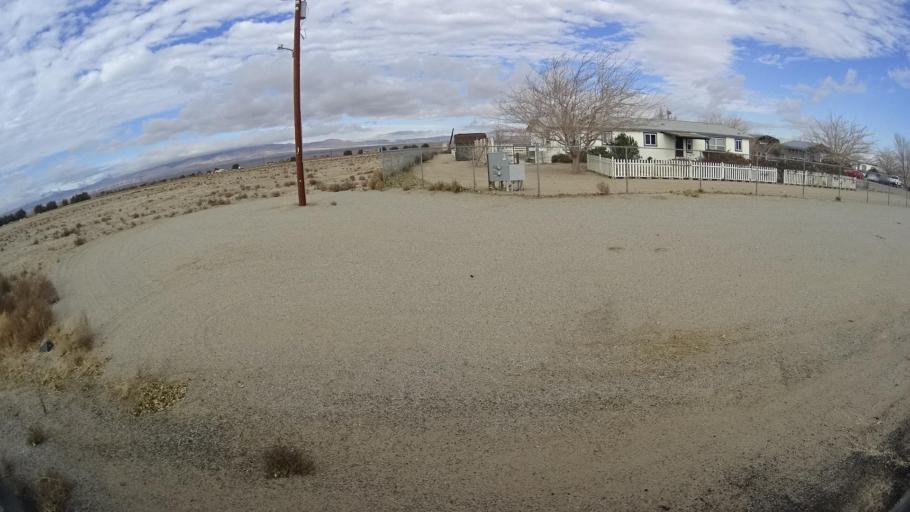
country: US
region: California
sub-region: Kern County
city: Rosamond
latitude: 34.8202
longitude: -118.3037
